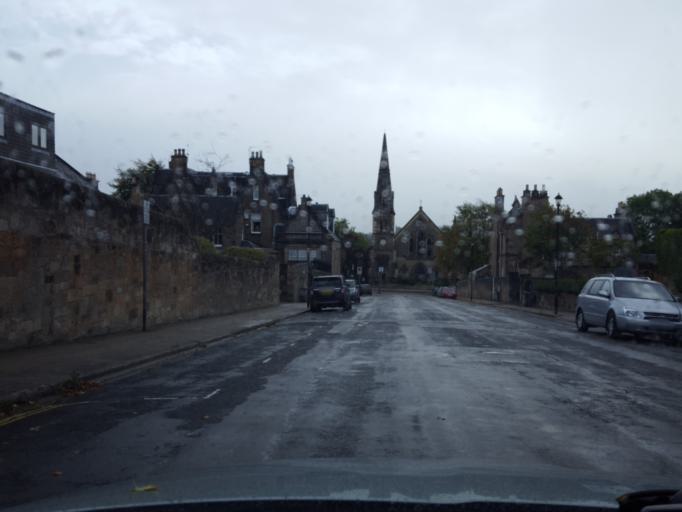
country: GB
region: Scotland
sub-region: Edinburgh
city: Edinburgh
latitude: 55.9468
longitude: -3.2295
